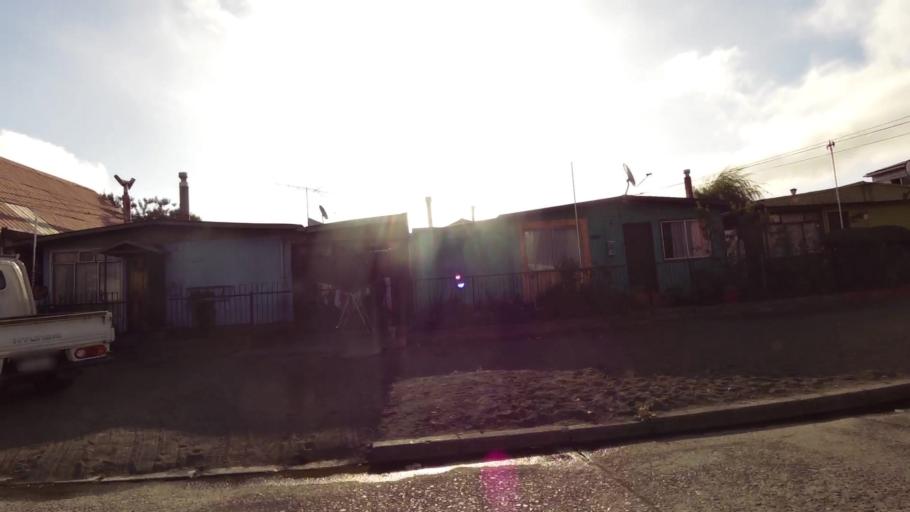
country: CL
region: Biobio
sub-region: Provincia de Concepcion
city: Concepcion
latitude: -36.7882
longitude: -73.0916
